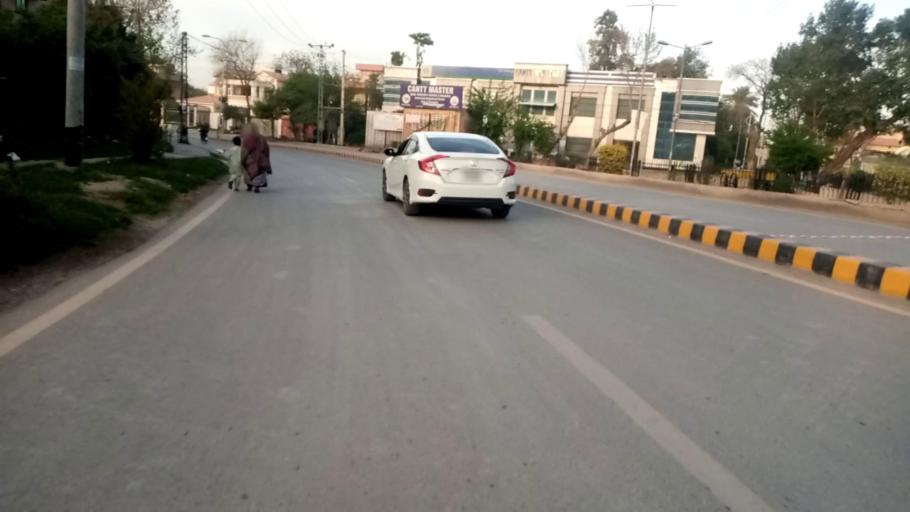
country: PK
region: Khyber Pakhtunkhwa
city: Peshawar
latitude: 34.0176
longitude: 71.5546
